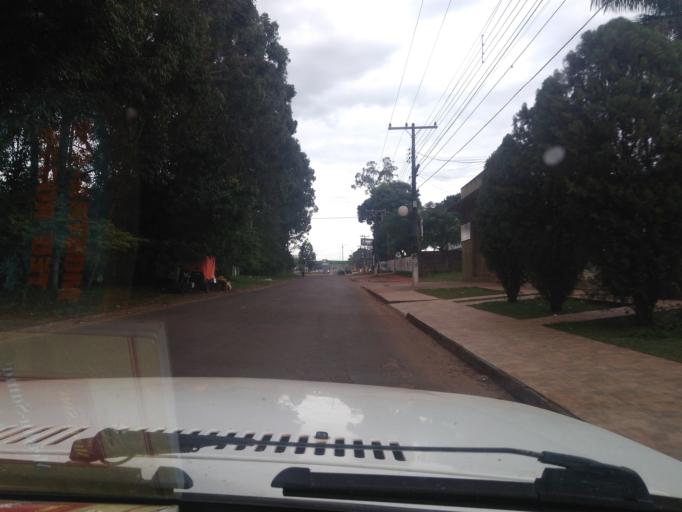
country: BR
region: Mato Grosso do Sul
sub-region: Ponta Pora
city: Ponta Pora
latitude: -22.5183
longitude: -55.7387
